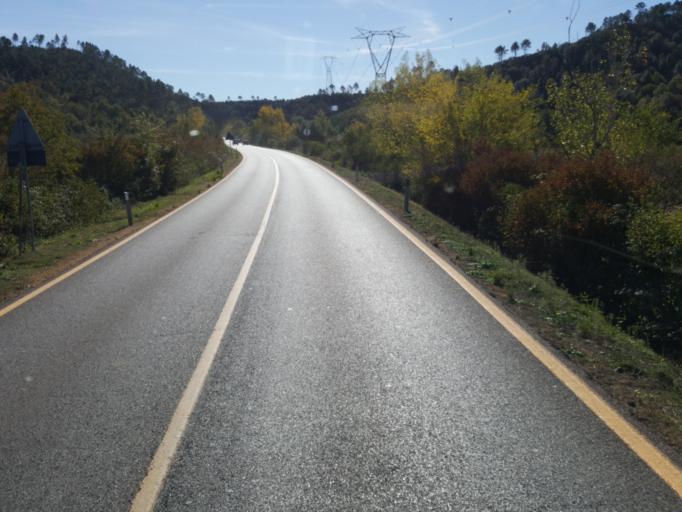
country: IT
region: Tuscany
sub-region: Provincia di Grosseto
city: Civitella Marittima
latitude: 43.0228
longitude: 11.2809
